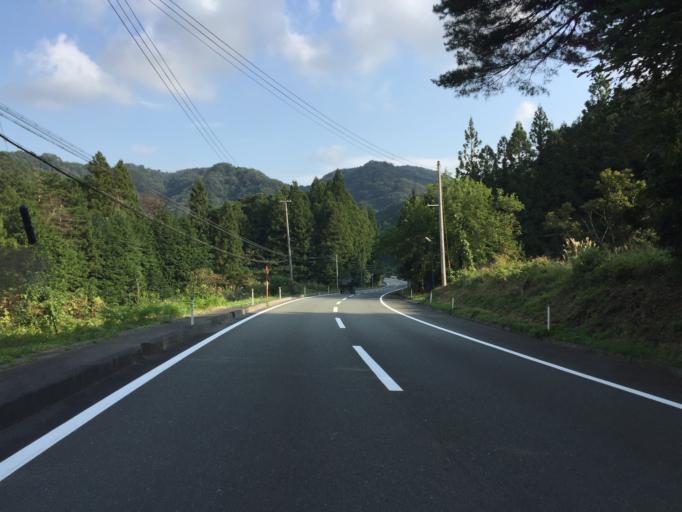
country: JP
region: Fukushima
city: Namie
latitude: 37.5084
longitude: 140.9089
